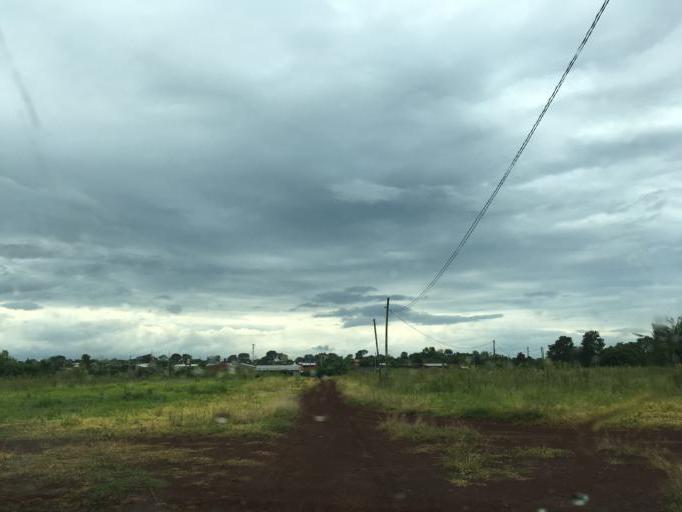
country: PY
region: Alto Parana
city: Ciudad del Este
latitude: -25.4270
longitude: -54.6543
